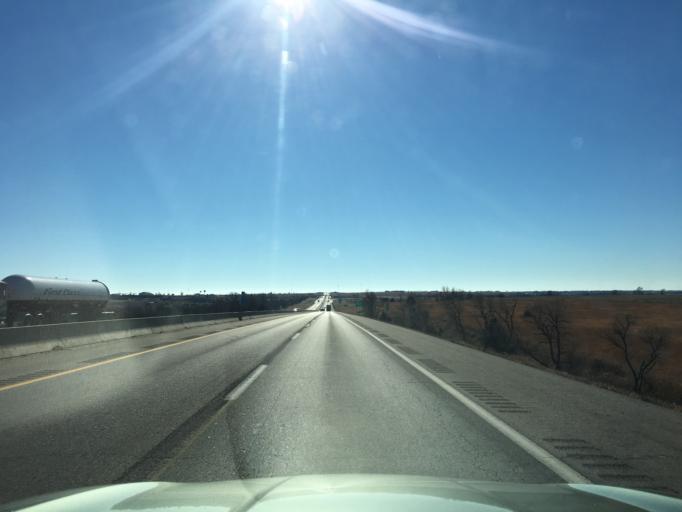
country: US
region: Kansas
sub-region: Sumner County
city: Wellington
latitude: 37.0717
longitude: -97.3386
